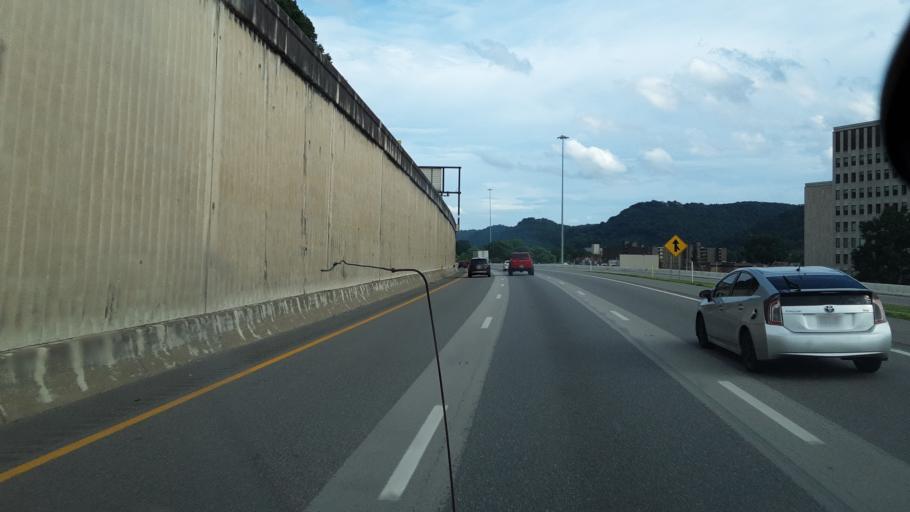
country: US
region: West Virginia
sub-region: Kanawha County
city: Charleston
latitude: 38.3399
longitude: -81.6117
